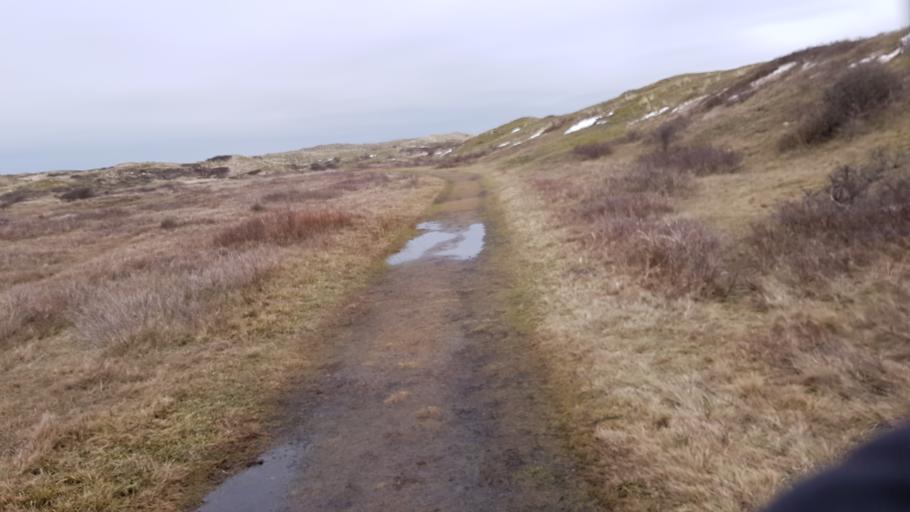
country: NL
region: North Holland
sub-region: Gemeente Bergen
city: Egmond aan Zee
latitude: 52.5840
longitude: 4.6173
